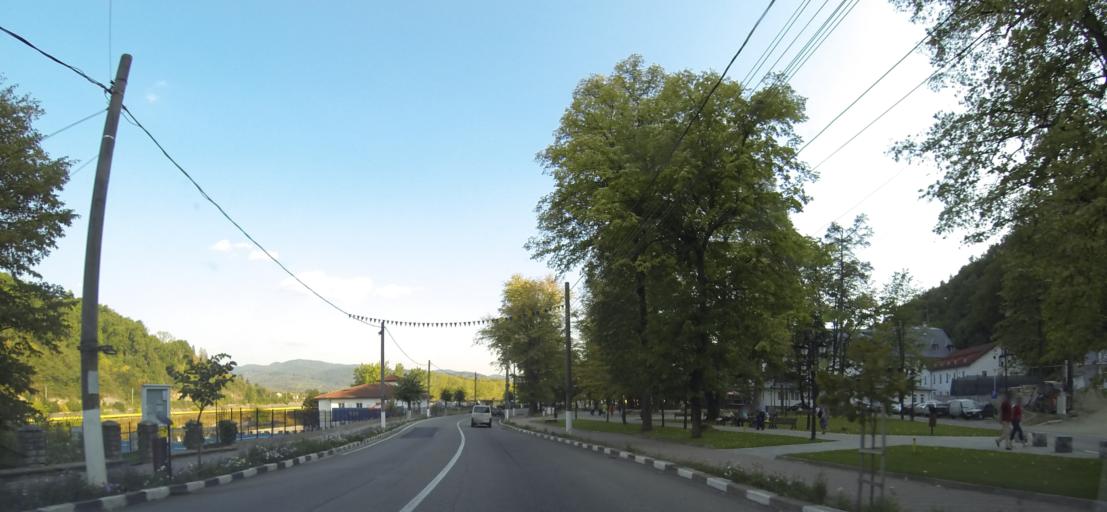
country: RO
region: Valcea
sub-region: Oras Calimanesti
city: Jiblea Veche
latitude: 45.2493
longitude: 24.3375
